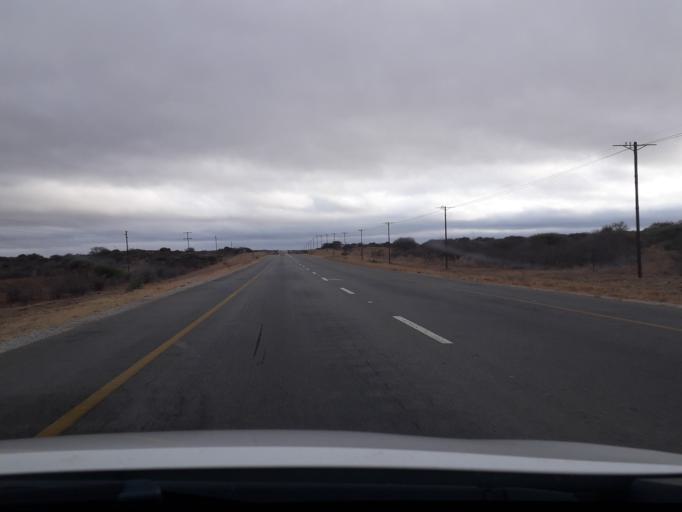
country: ZA
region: Limpopo
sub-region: Capricorn District Municipality
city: Polokwane
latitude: -23.6597
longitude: 29.6132
